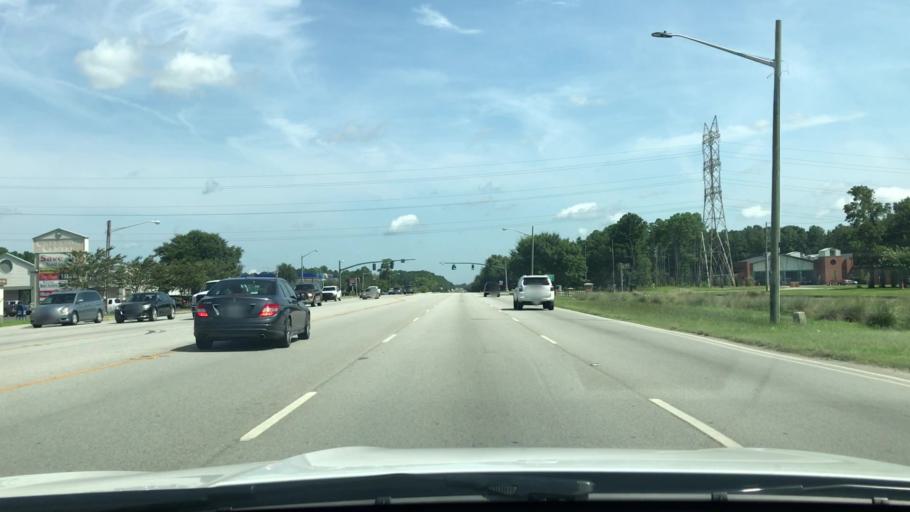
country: US
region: South Carolina
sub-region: Berkeley County
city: Goose Creek
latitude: 33.0021
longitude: -80.0379
